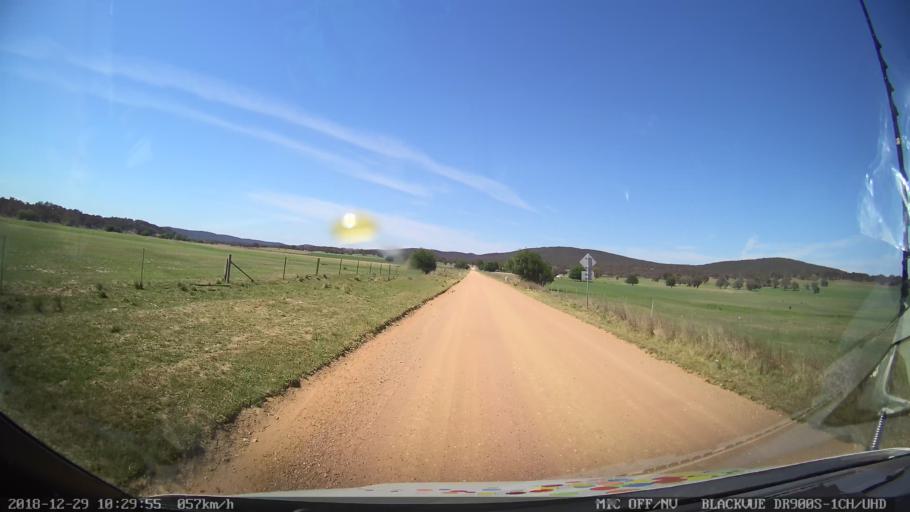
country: AU
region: New South Wales
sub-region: Yass Valley
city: Gundaroo
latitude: -34.9559
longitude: 149.4557
